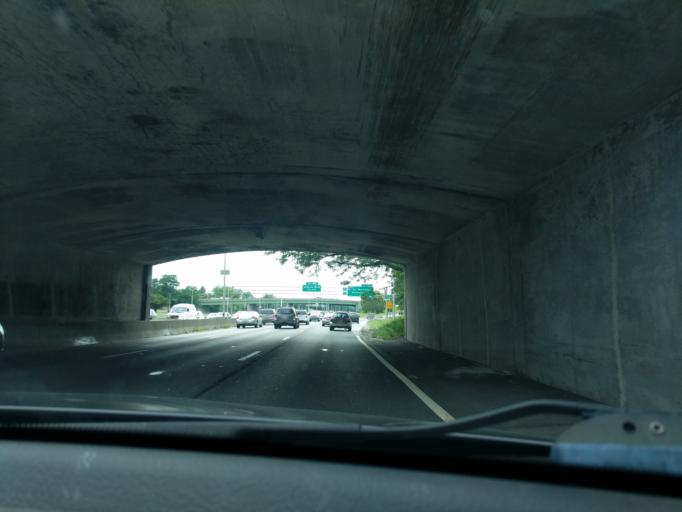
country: US
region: New York
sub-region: Queens County
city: Jamaica
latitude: 40.6665
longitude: -73.7892
